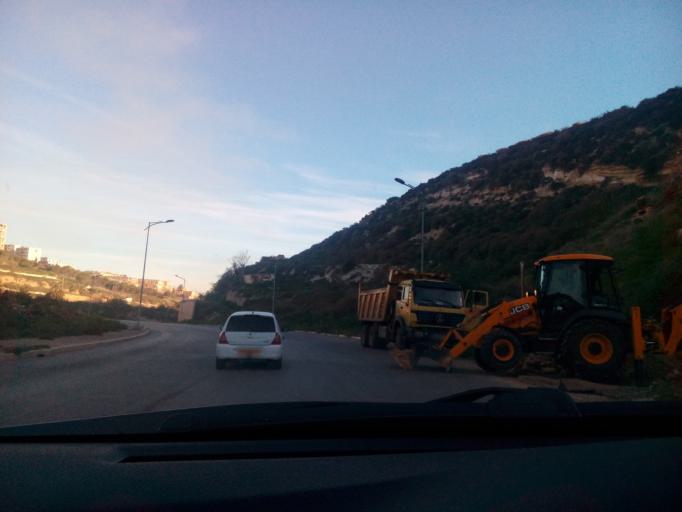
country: DZ
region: Oran
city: Oran
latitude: 35.6965
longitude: -0.6566
